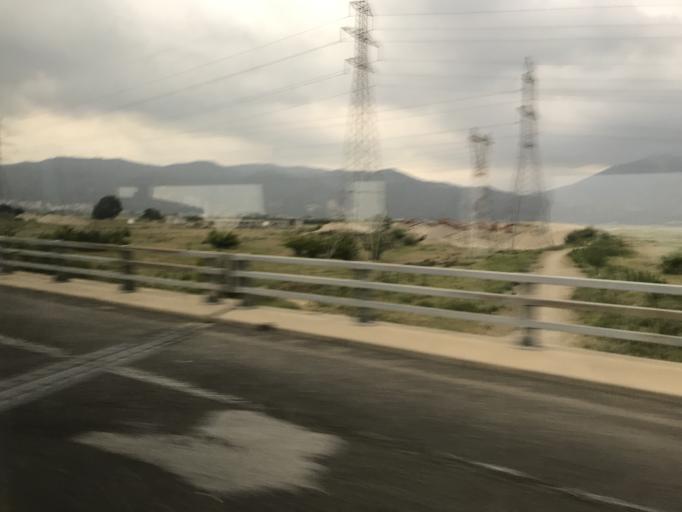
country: GR
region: East Macedonia and Thrace
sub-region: Nomos Rodopis
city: Iasmos
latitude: 41.1131
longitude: 25.2088
